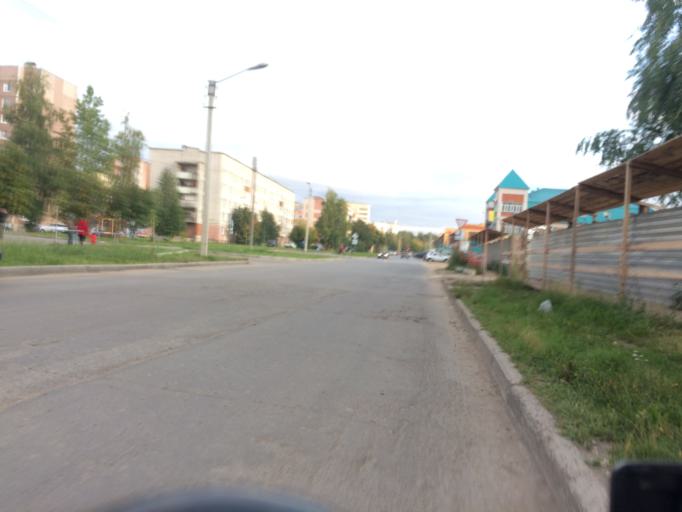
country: RU
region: Mariy-El
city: Medvedevo
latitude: 56.6451
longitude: 47.8348
